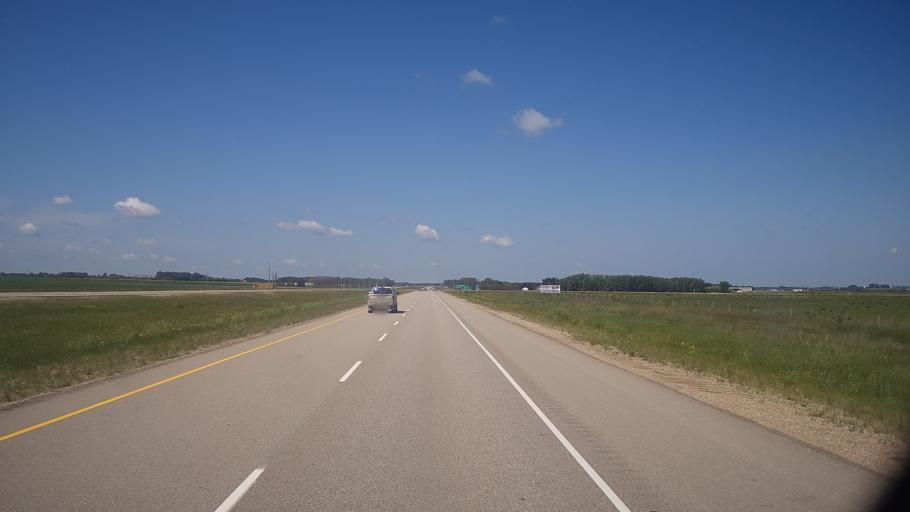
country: CA
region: Saskatchewan
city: Saskatoon
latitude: 52.0123
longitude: -106.3752
